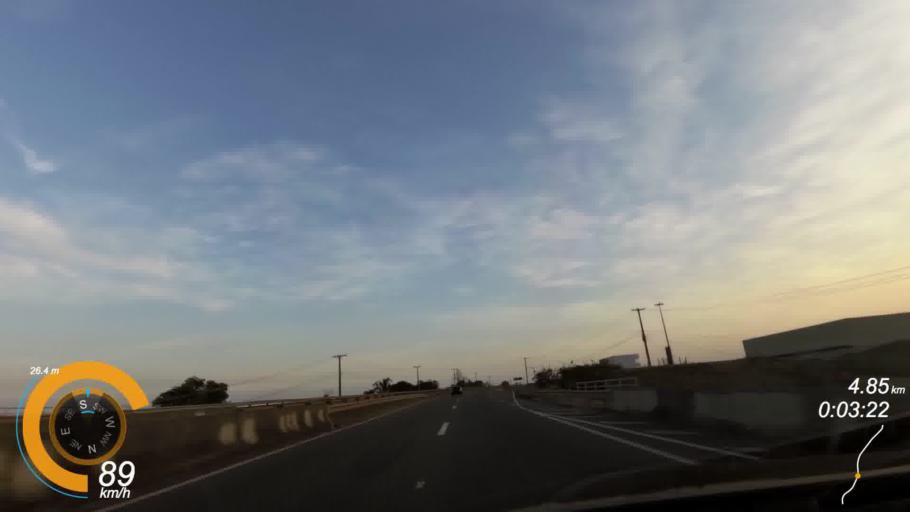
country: BR
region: Espirito Santo
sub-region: Vitoria
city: Vitoria
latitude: -20.4857
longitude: -40.3528
